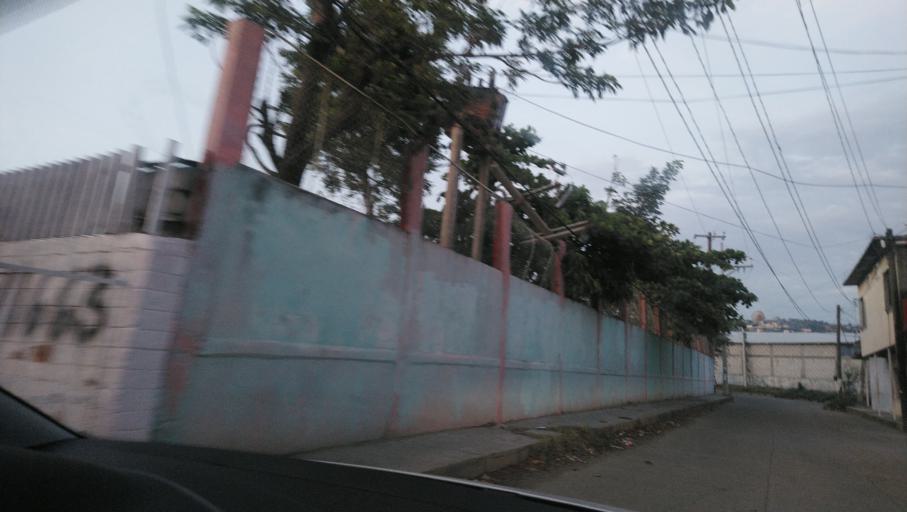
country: MX
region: Oaxaca
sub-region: Salina Cruz
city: Salina Cruz
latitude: 16.1770
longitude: -95.1957
